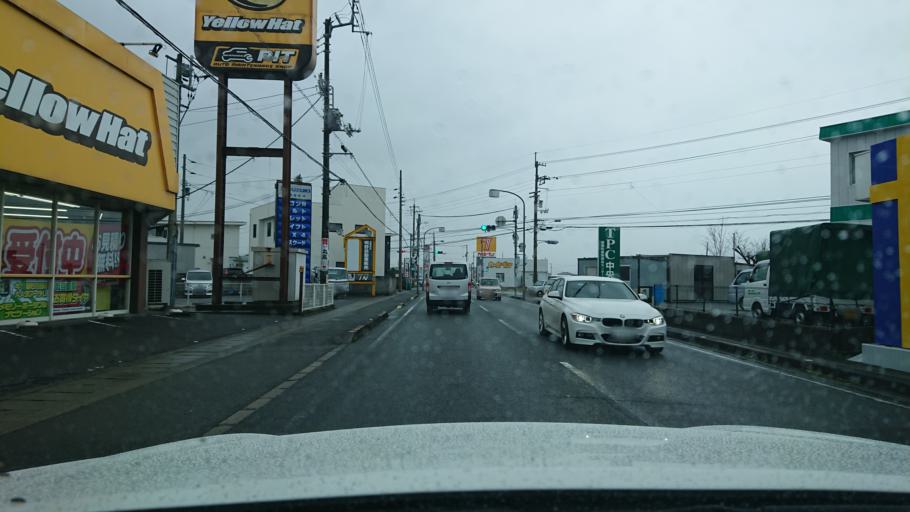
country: JP
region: Tokushima
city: Ishii
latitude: 34.0855
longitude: 134.4937
